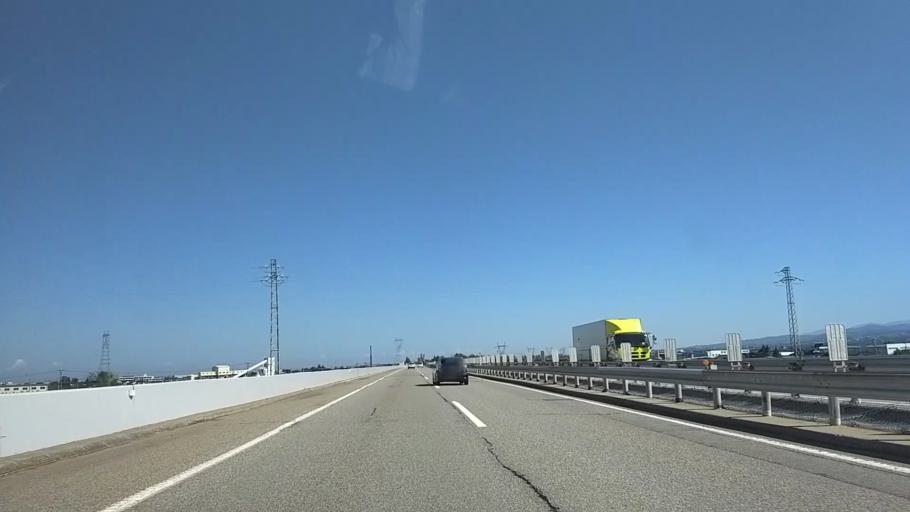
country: JP
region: Toyama
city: Kamiichi
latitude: 36.6982
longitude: 137.3324
